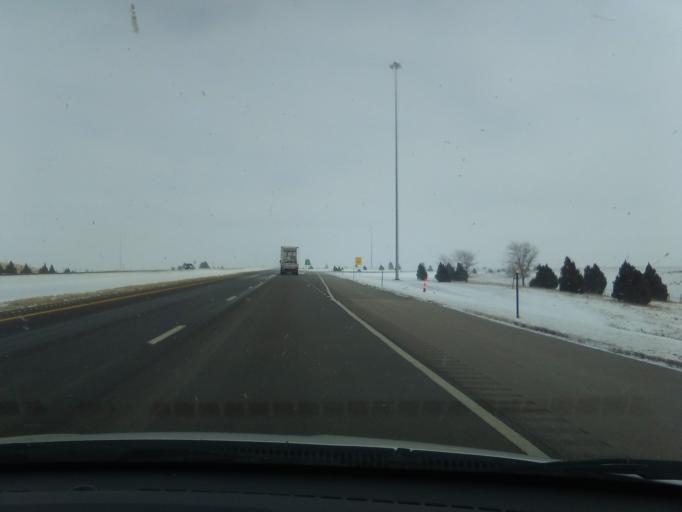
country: US
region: Nebraska
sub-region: Kimball County
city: Kimball
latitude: 41.2196
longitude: -103.6323
